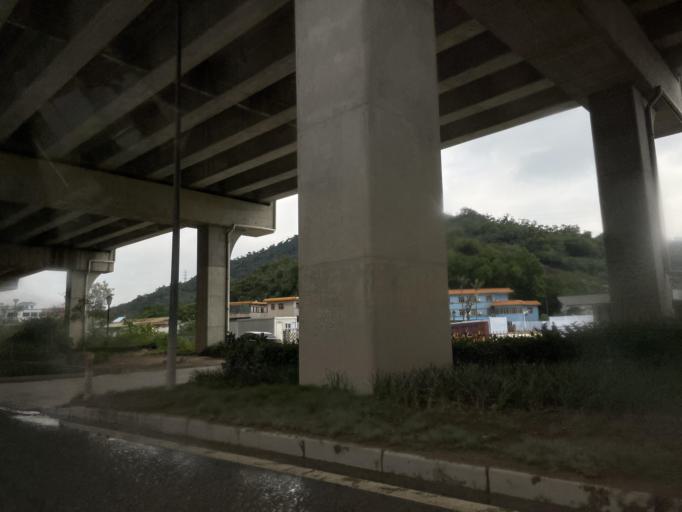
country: CN
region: Guangdong
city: Nanping
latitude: 22.1802
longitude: 113.4629
